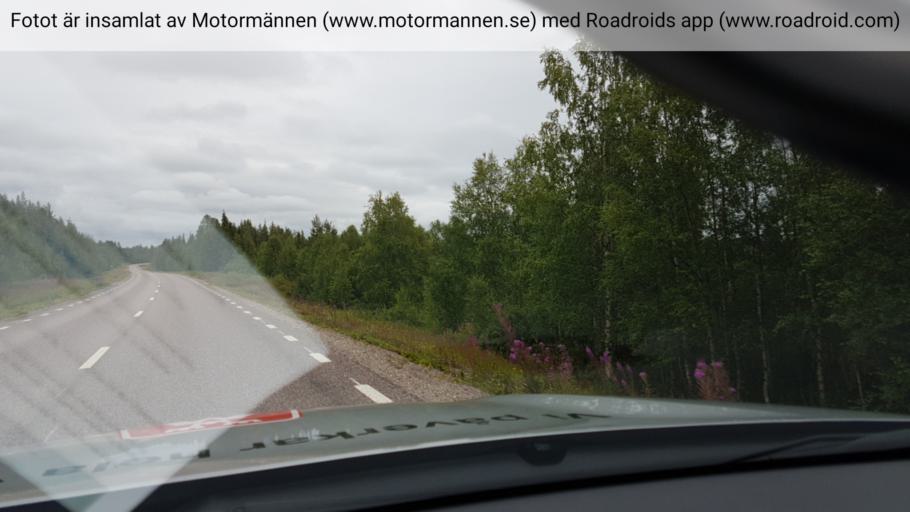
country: SE
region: Norrbotten
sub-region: Gallivare Kommun
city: Gaellivare
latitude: 67.0743
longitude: 21.3913
